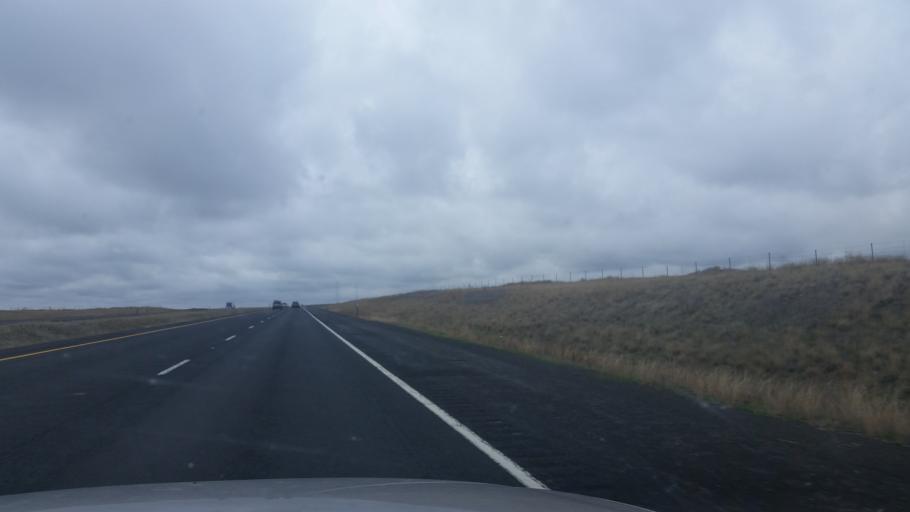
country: US
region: Washington
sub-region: Spokane County
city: Medical Lake
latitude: 47.3329
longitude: -117.9199
